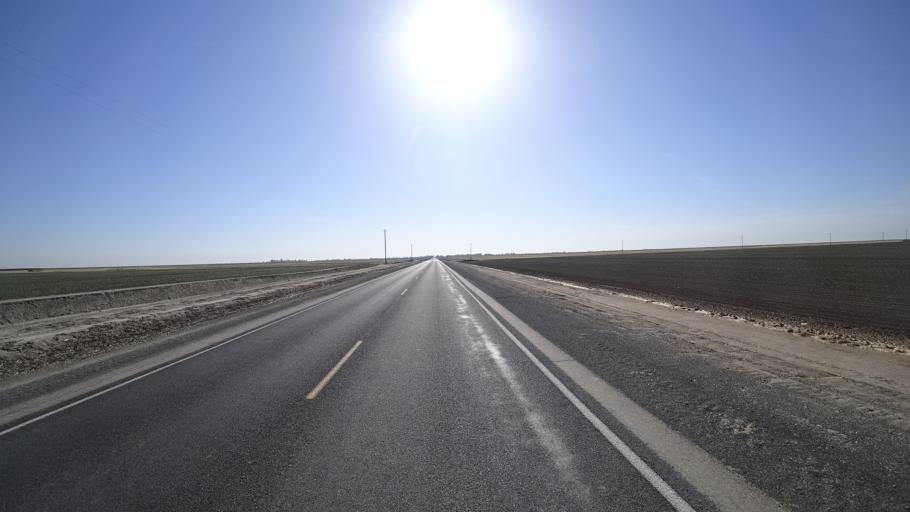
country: US
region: California
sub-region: Kings County
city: Corcoran
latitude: 36.0980
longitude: -119.6285
